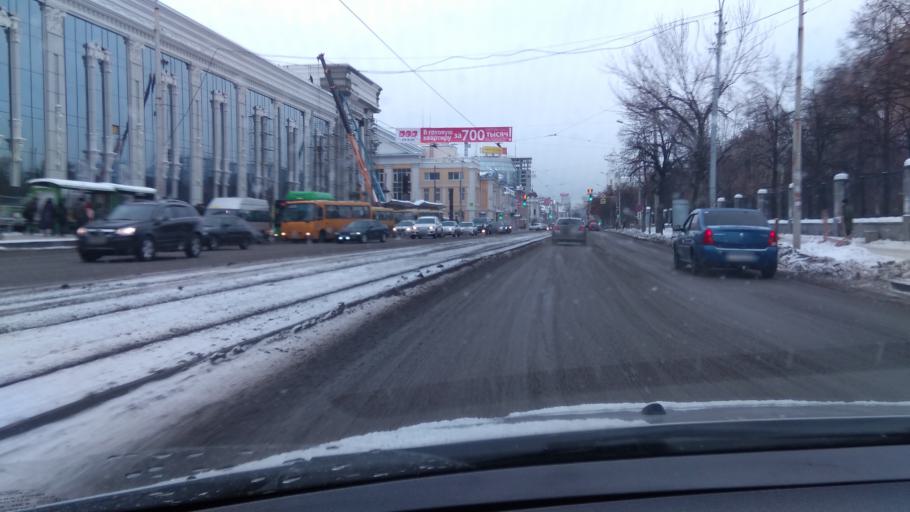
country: RU
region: Sverdlovsk
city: Yekaterinburg
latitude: 56.8278
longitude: 60.6021
